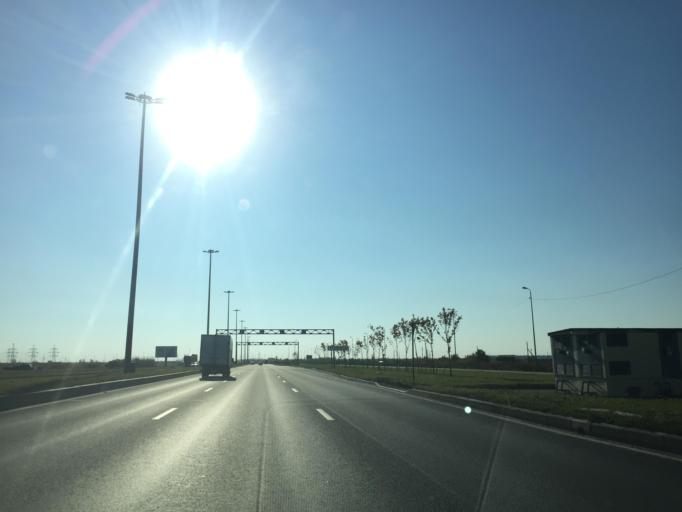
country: RU
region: St.-Petersburg
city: Petro-Slavyanka
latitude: 59.7733
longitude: 30.4994
